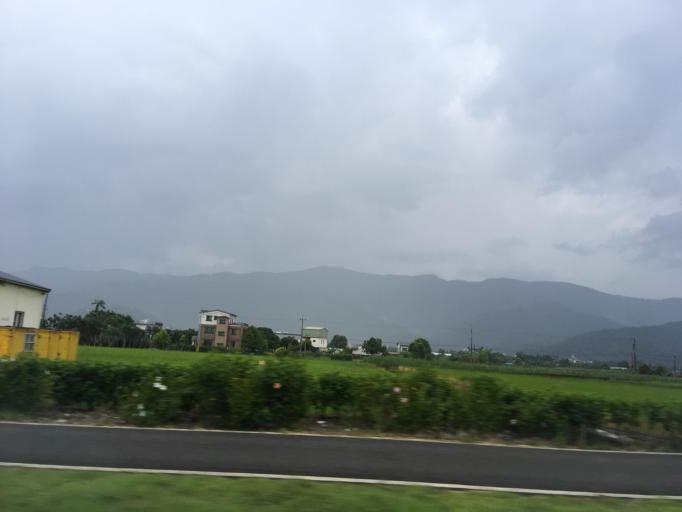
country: TW
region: Taiwan
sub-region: Yilan
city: Yilan
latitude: 24.6772
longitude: 121.6526
